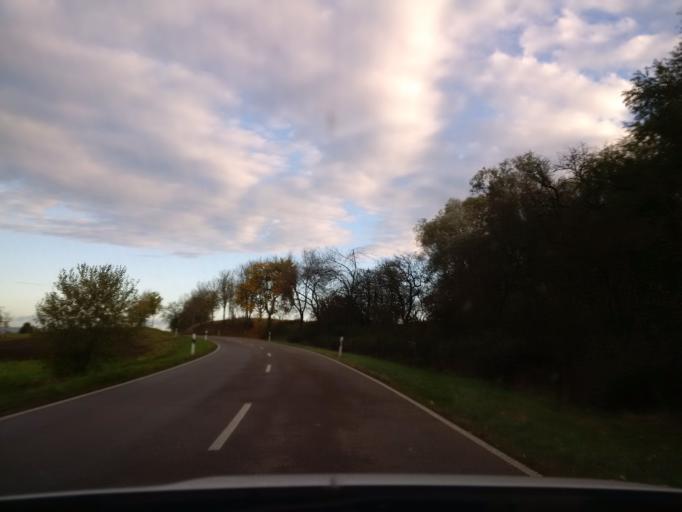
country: DE
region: Baden-Wuerttemberg
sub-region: Tuebingen Region
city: Achstetten
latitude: 48.2701
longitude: 9.9042
